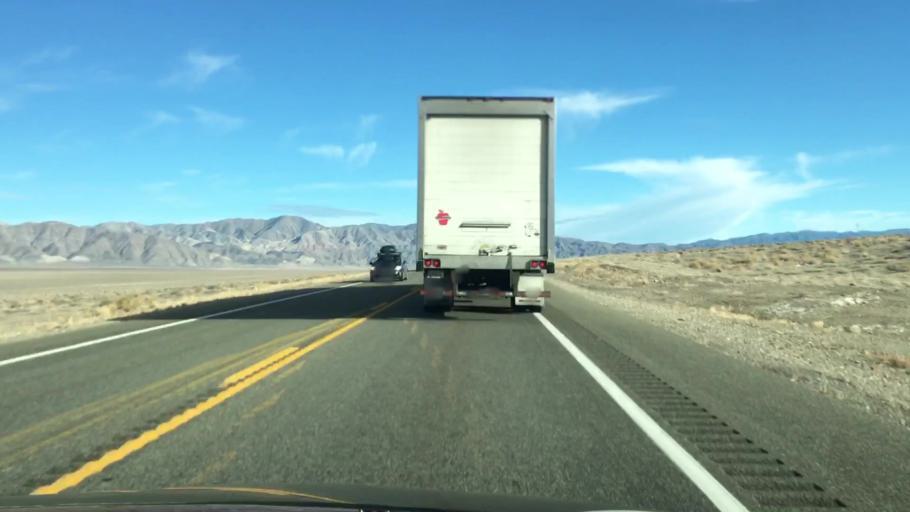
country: US
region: Nevada
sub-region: Mineral County
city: Hawthorne
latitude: 38.5316
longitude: -118.2779
